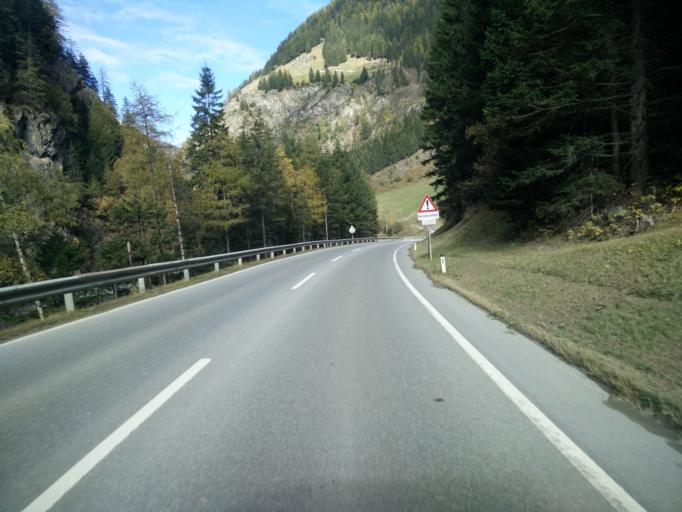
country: AT
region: Tyrol
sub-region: Politischer Bezirk Imst
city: Soelden
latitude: 47.0364
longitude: 10.9857
